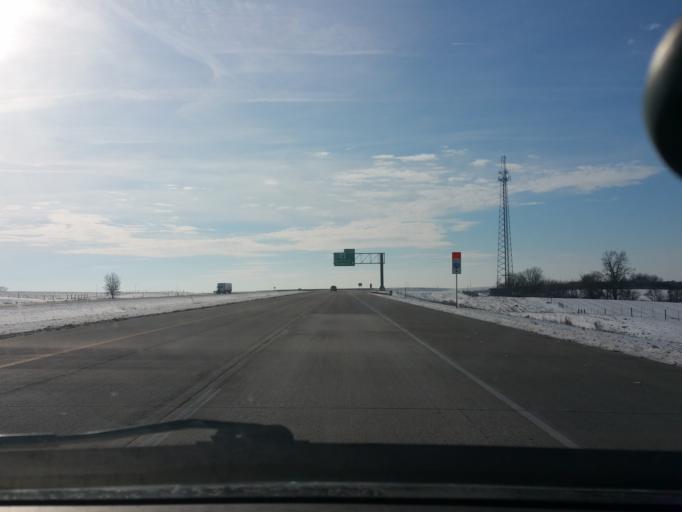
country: US
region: Iowa
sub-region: Warren County
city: Norwalk
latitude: 41.4908
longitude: -93.7805
